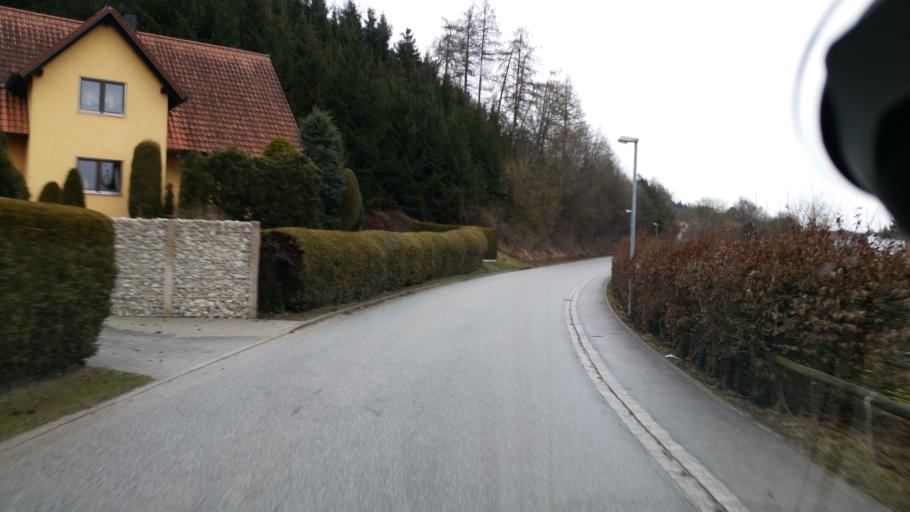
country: DE
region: Bavaria
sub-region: Lower Bavaria
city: Eching
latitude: 48.4978
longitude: 12.0644
